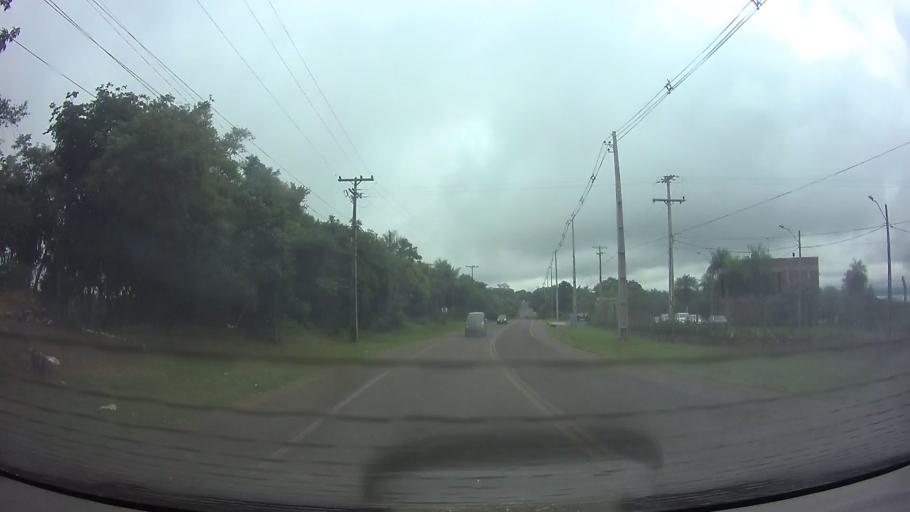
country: PY
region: Cordillera
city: Altos
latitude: -25.2866
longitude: -57.2638
